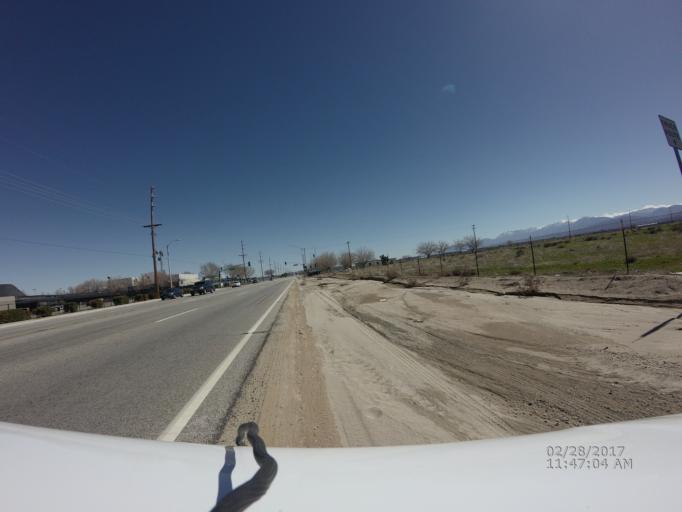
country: US
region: California
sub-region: Los Angeles County
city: Palmdale
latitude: 34.6023
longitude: -118.0865
